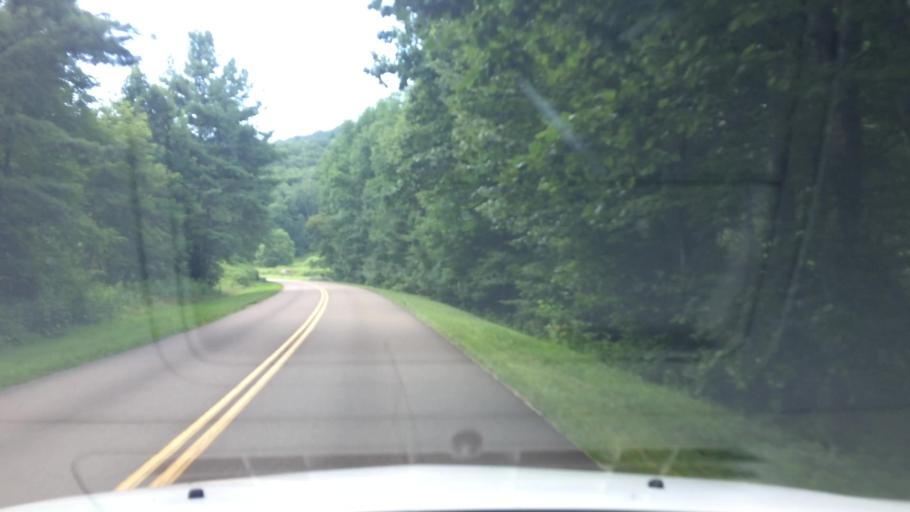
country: US
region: North Carolina
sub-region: Watauga County
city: Blowing Rock
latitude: 36.1559
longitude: -81.6695
